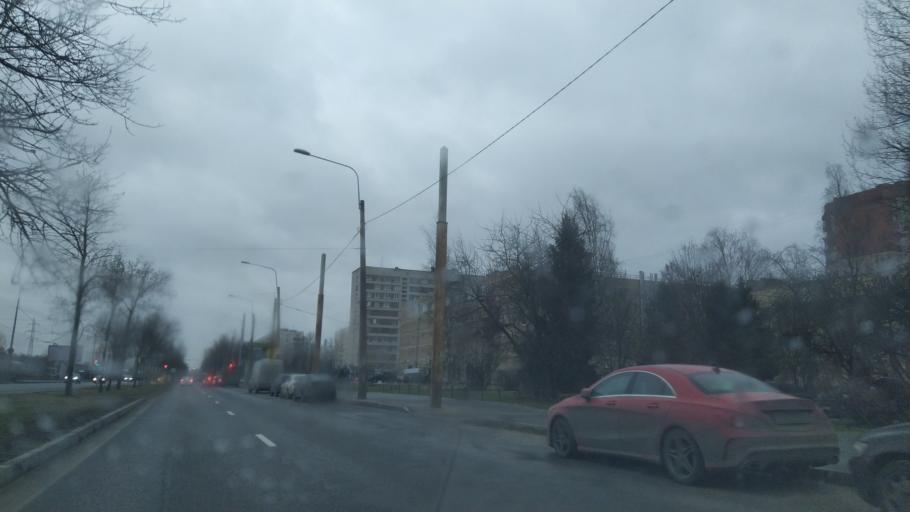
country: RU
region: St.-Petersburg
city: Grazhdanka
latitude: 60.0198
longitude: 30.4147
